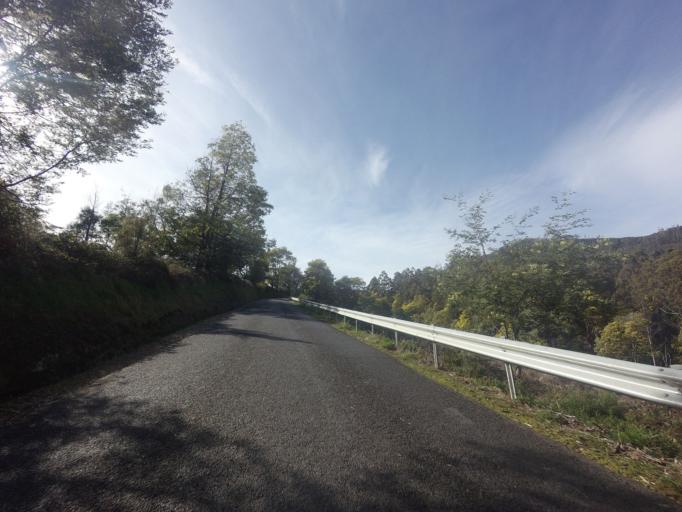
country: AU
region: Tasmania
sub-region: Kingborough
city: Kettering
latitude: -43.1738
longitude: 147.1651
